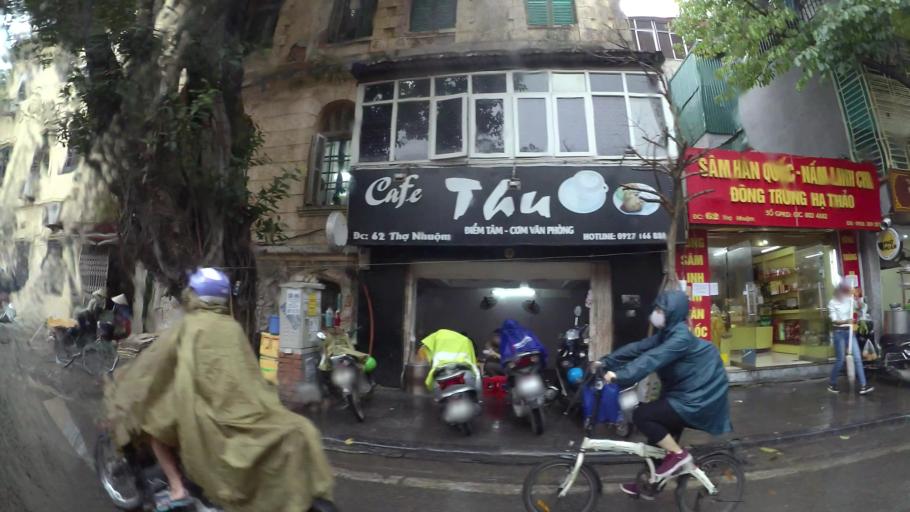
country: VN
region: Ha Noi
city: Hanoi
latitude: 21.0250
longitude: 105.8461
